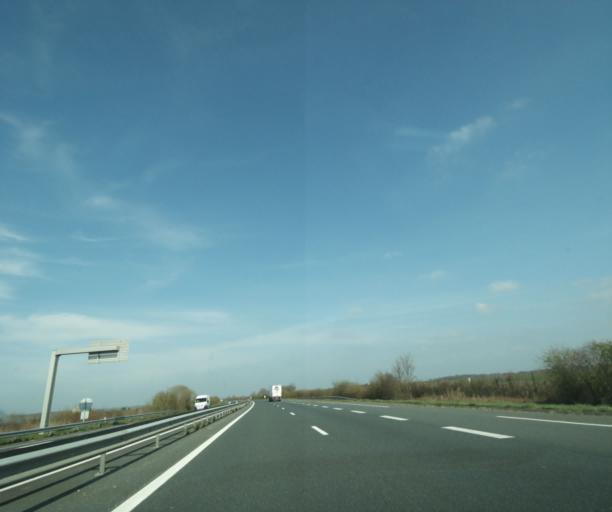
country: FR
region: Centre
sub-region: Departement de l'Indre
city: Saint-Marcel
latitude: 46.6534
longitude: 1.5642
